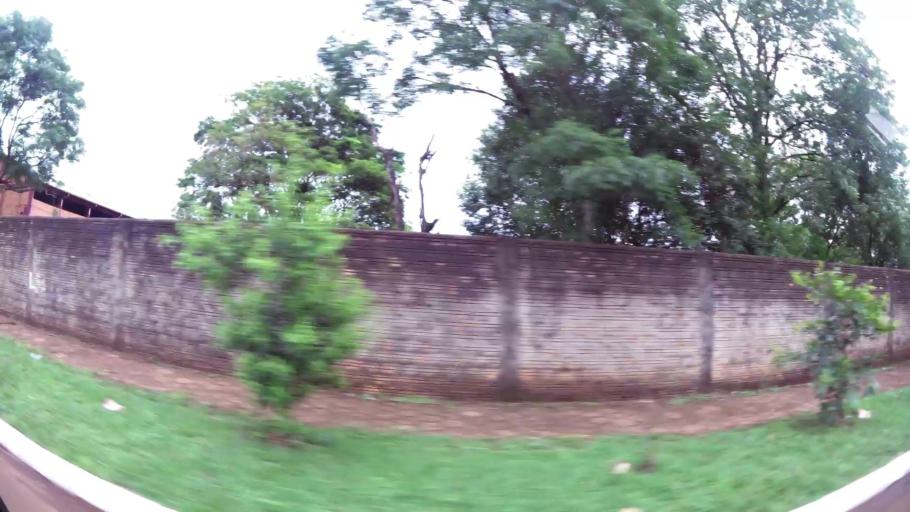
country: PY
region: Alto Parana
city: Ciudad del Este
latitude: -25.4841
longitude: -54.7605
